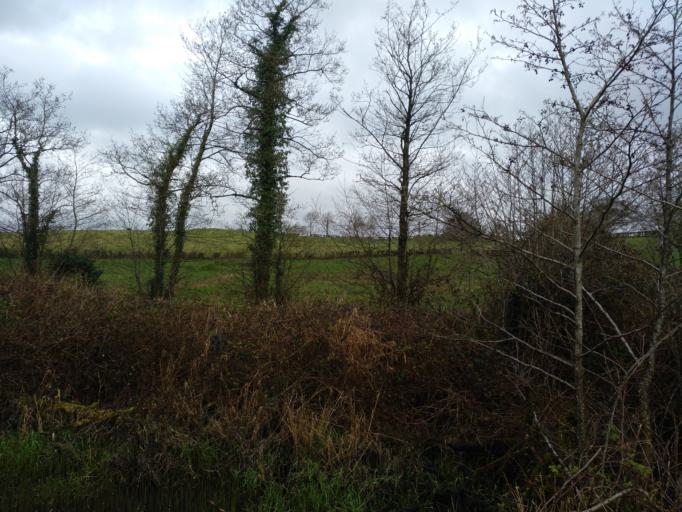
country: IE
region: Ulster
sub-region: County Monaghan
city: Clones
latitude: 54.1813
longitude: -7.1980
